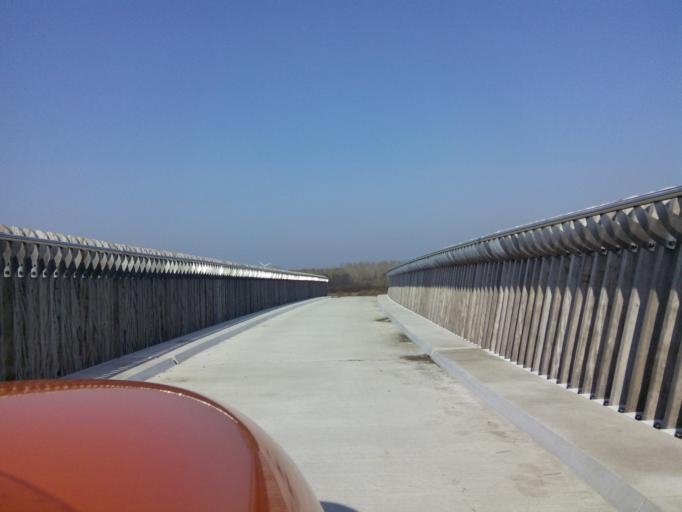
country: NL
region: Flevoland
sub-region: Gemeente Zeewolde
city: Zeewolde
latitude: 52.3253
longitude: 5.4486
